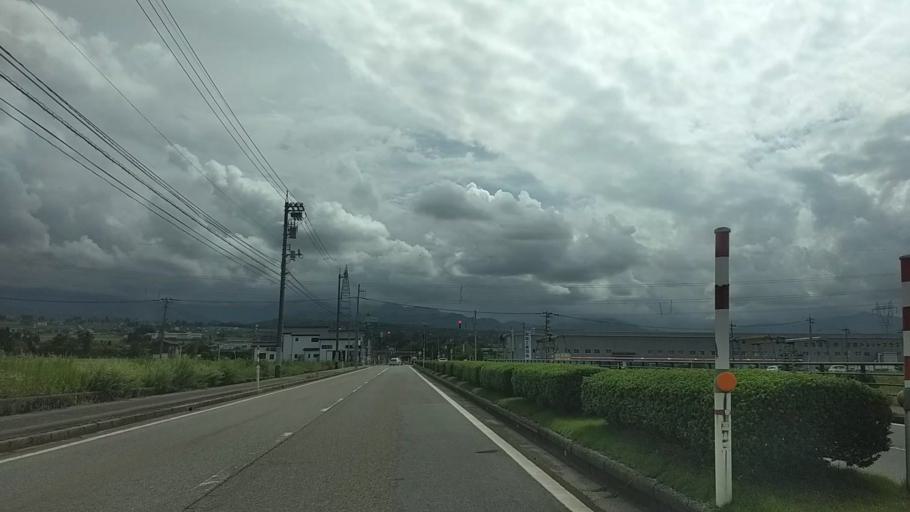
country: JP
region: Toyama
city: Namerikawa
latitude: 36.7466
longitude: 137.3760
